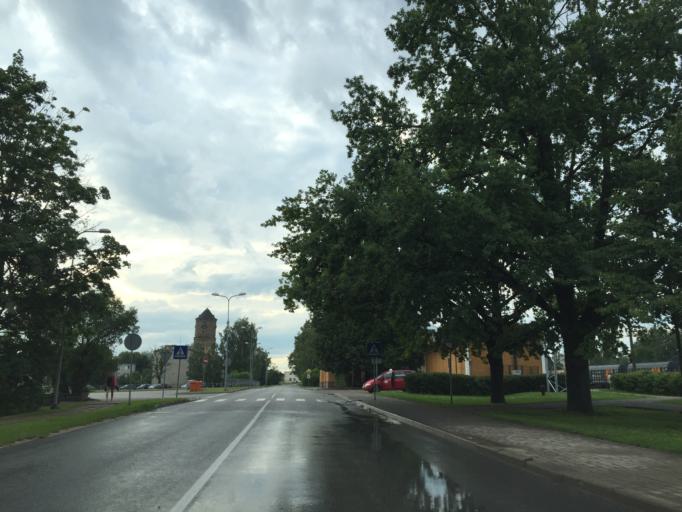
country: LV
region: Dobeles Rajons
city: Dobele
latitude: 56.6279
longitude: 23.2856
